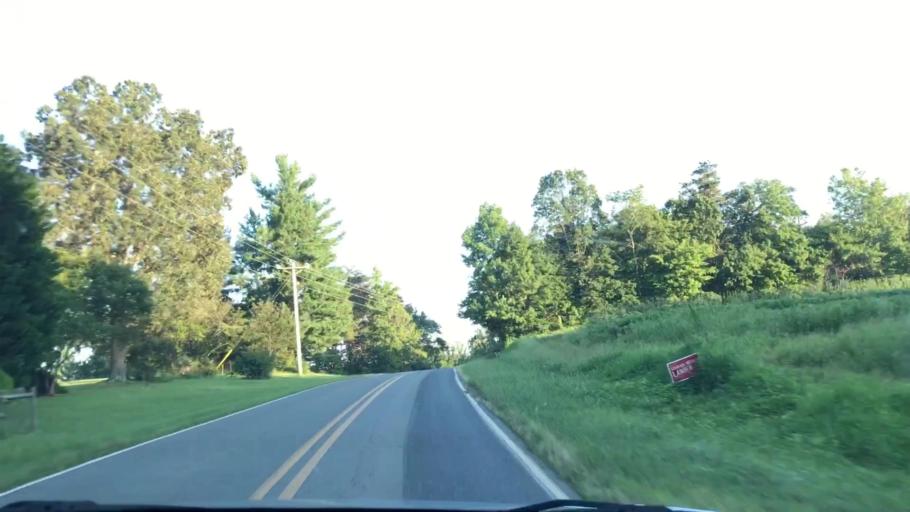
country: US
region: North Carolina
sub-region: Randolph County
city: Franklinville
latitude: 35.8052
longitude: -79.6824
